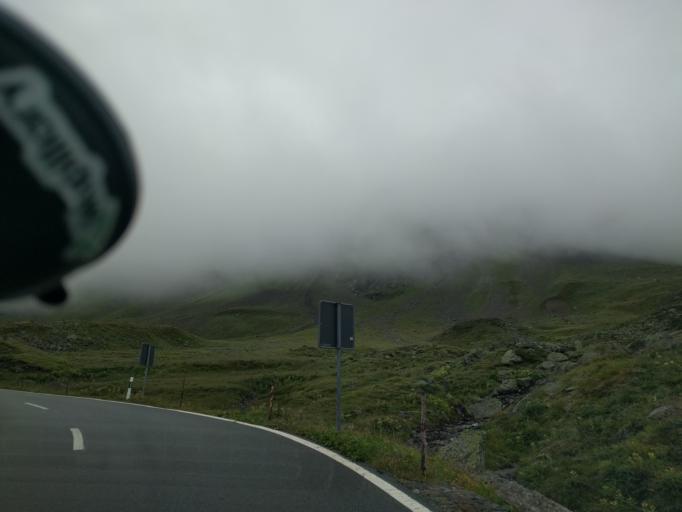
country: CH
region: Grisons
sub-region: Praettigau/Davos District
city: Davos
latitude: 46.7607
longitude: 9.9398
